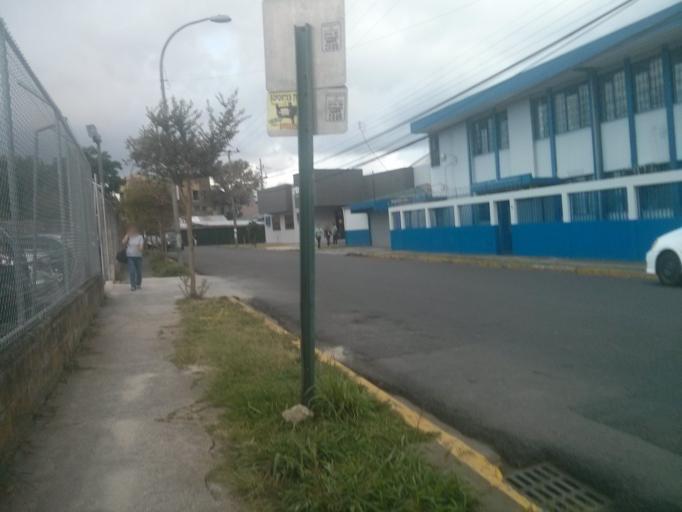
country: CR
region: San Jose
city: Calle Blancos
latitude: 9.9364
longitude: -84.0661
